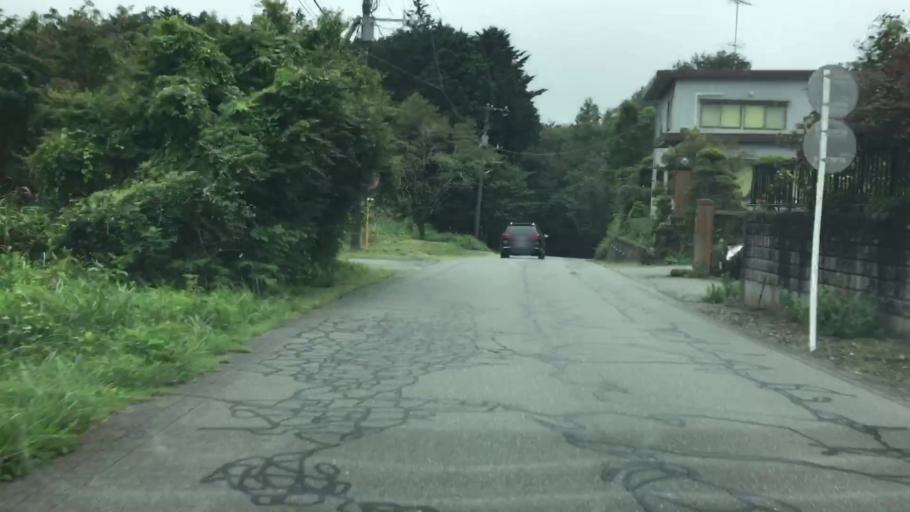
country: JP
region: Shizuoka
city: Fujinomiya
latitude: 35.3601
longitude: 138.5906
